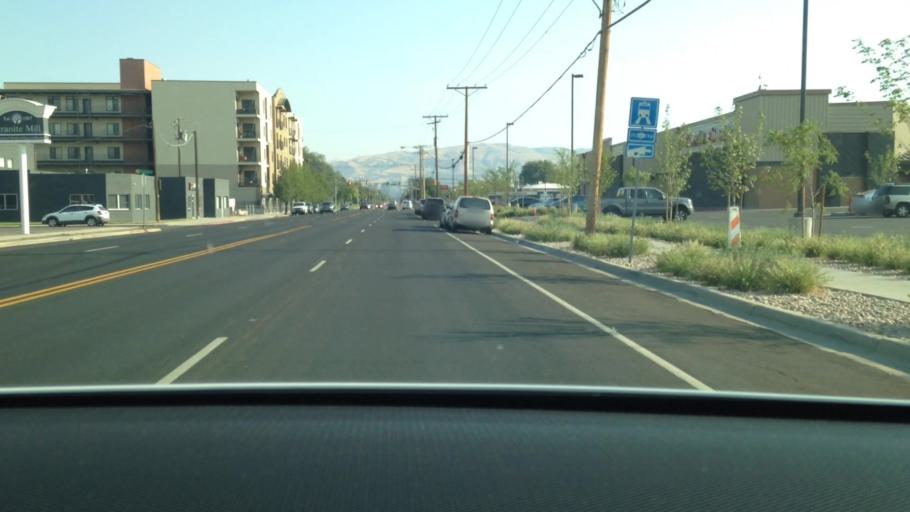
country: US
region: Utah
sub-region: Salt Lake County
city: South Salt Lake
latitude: 40.7232
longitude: -111.8911
